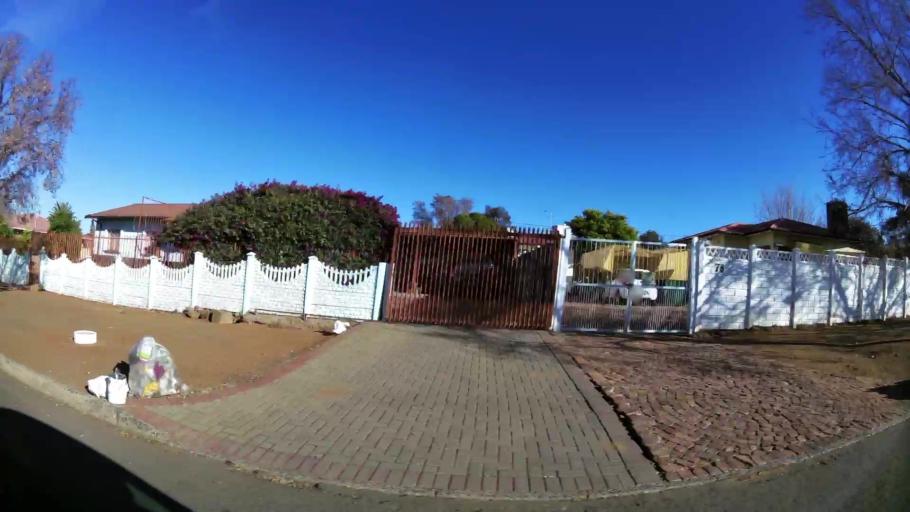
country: ZA
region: Northern Cape
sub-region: Frances Baard District Municipality
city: Kimberley
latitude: -28.7520
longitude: 24.7900
